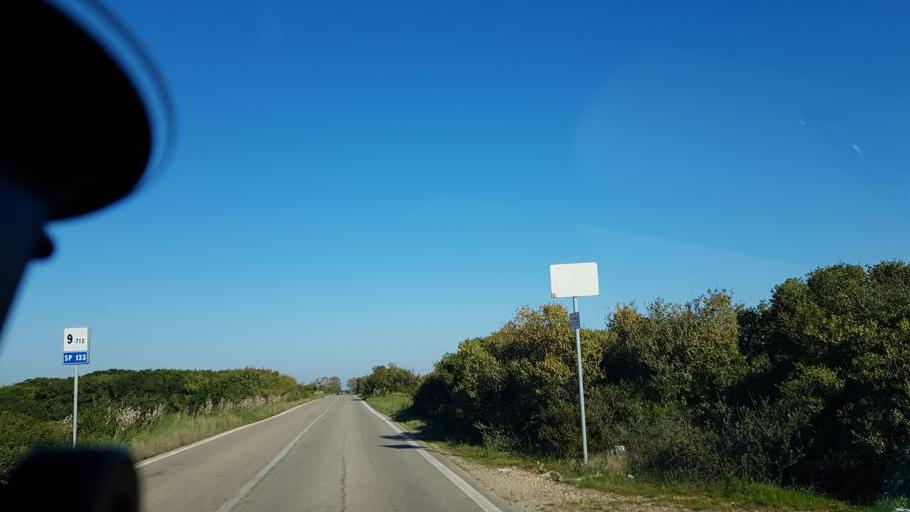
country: IT
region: Apulia
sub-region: Provincia di Lecce
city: Giorgilorio
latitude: 40.4563
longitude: 18.2052
